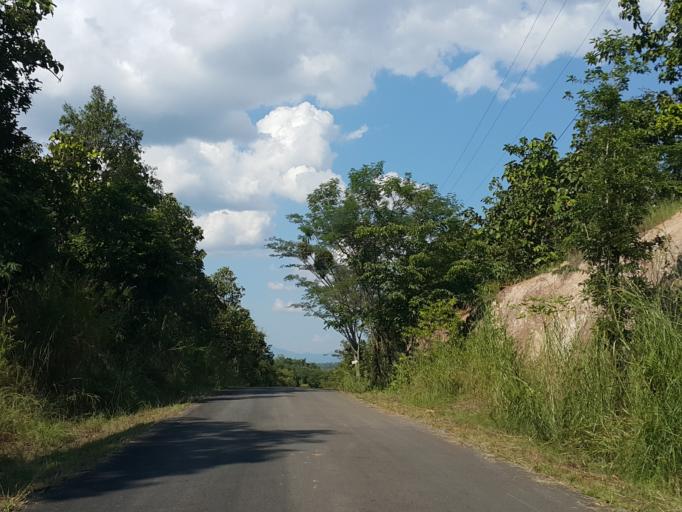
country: TH
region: Chiang Mai
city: San Sai
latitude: 18.9398
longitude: 98.9184
